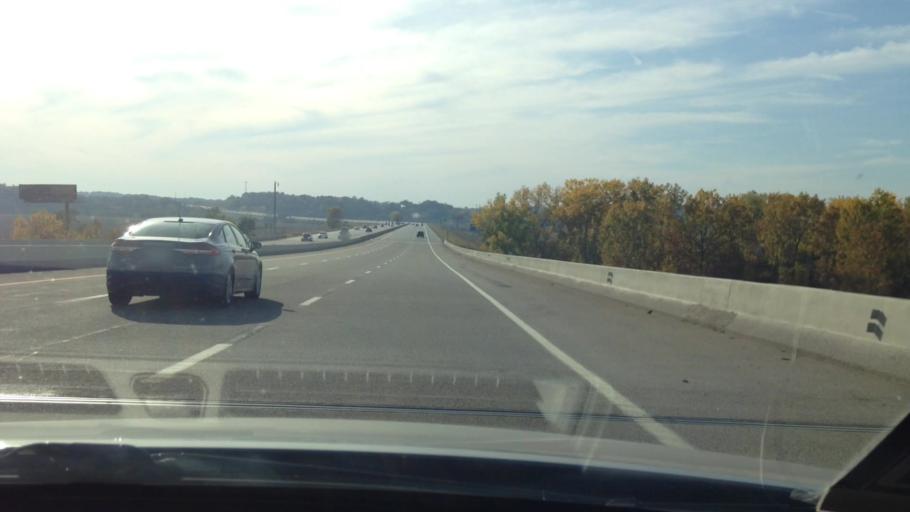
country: US
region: Missouri
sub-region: Platte County
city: Weatherby Lake
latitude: 39.1914
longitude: -94.7733
